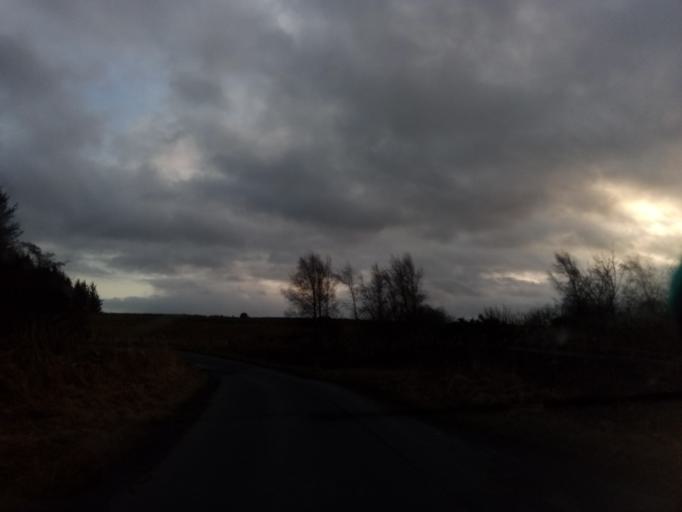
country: GB
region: Scotland
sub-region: The Scottish Borders
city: Selkirk
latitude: 55.5545
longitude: -2.7848
